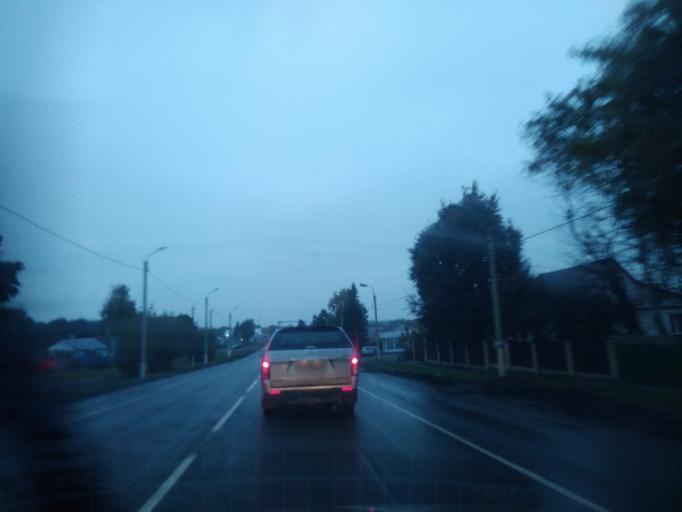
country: RU
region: Tula
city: Teploye
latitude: 53.6168
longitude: 37.5972
